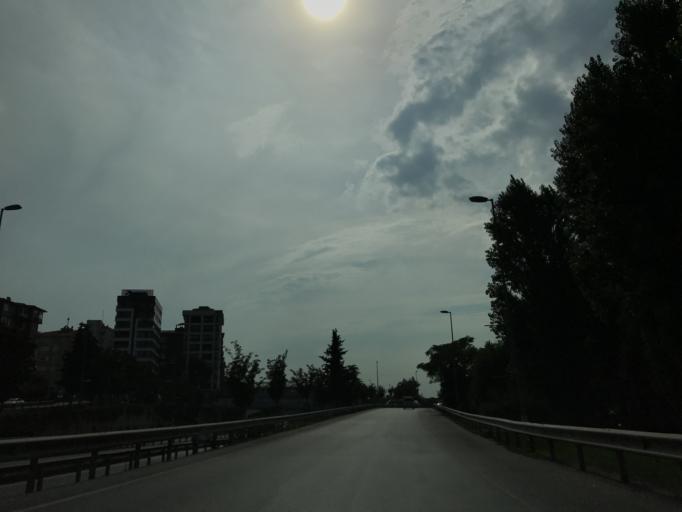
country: TR
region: Istanbul
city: UEskuedar
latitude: 40.9915
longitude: 29.0418
